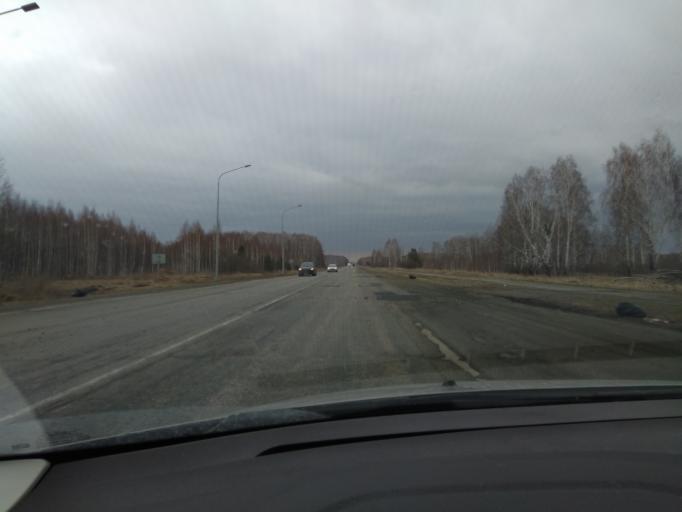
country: RU
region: Chelyabinsk
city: Tyubuk
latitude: 55.9834
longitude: 61.0241
